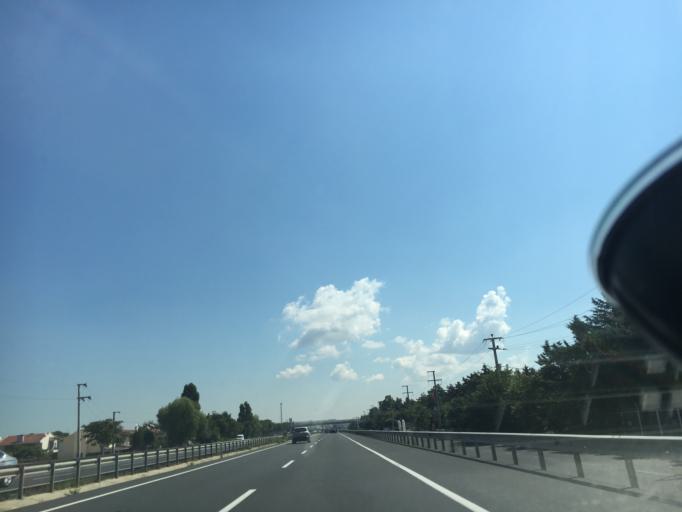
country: TR
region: Istanbul
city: Canta
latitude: 41.0530
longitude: 28.0608
